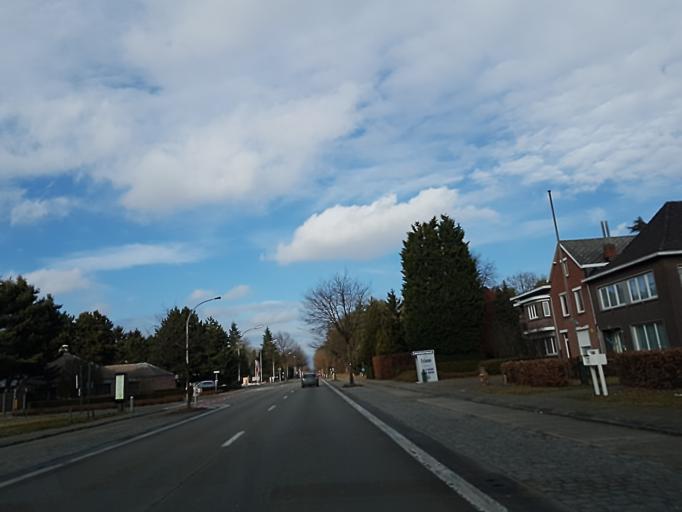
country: BE
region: Flanders
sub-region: Provincie Antwerpen
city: Mol
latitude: 51.1984
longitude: 5.1157
